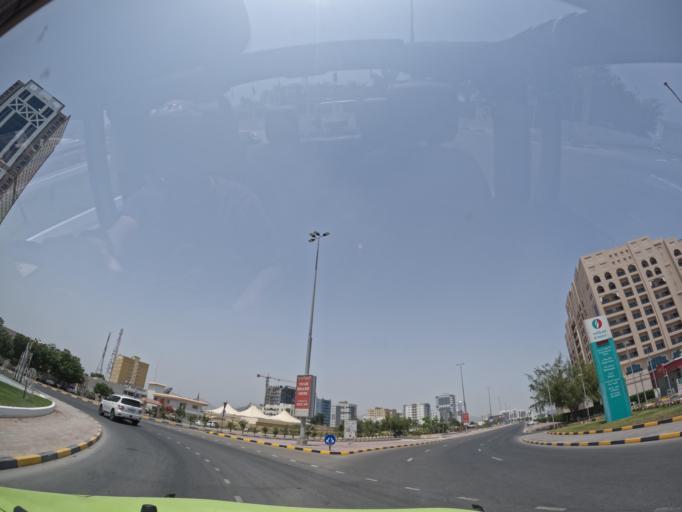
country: AE
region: Al Fujayrah
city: Al Fujayrah
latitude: 25.1281
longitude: 56.3564
